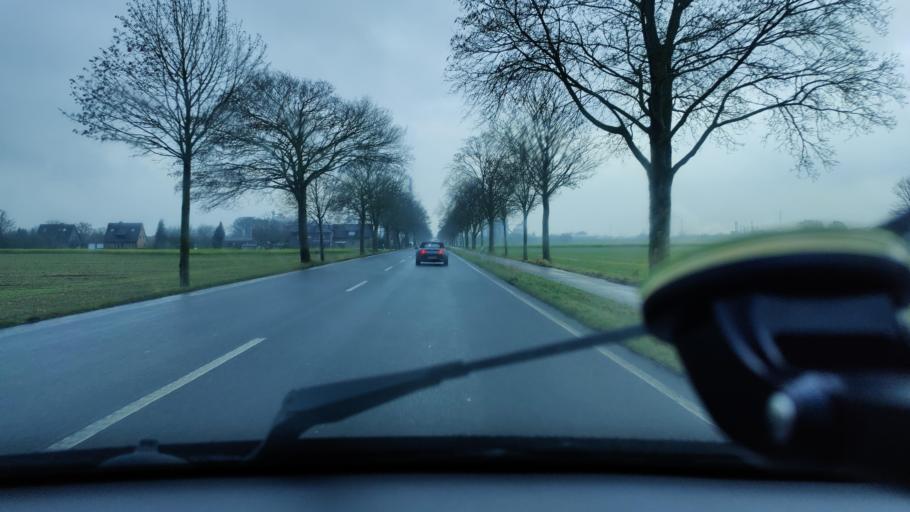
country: DE
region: North Rhine-Westphalia
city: Rheinberg
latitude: 51.5714
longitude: 6.5679
